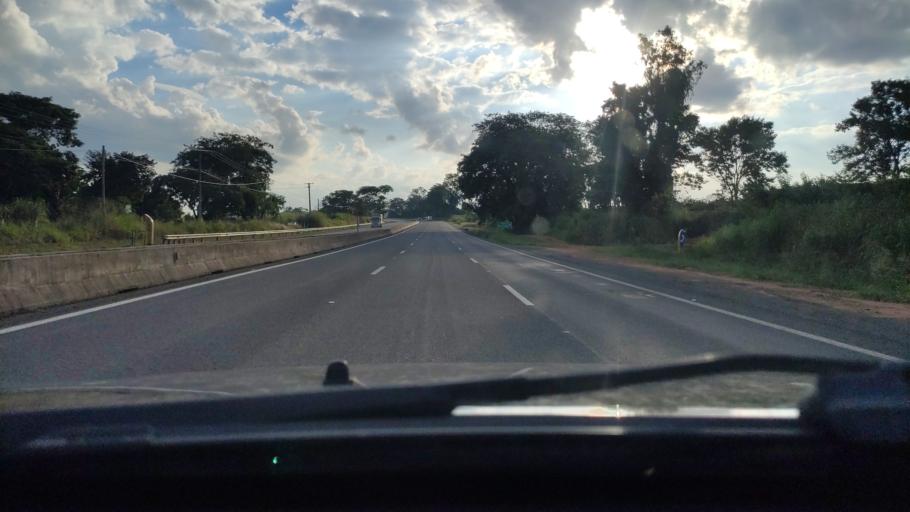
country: BR
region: Sao Paulo
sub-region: Mogi-Mirim
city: Mogi Mirim
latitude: -22.4506
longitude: -47.0789
